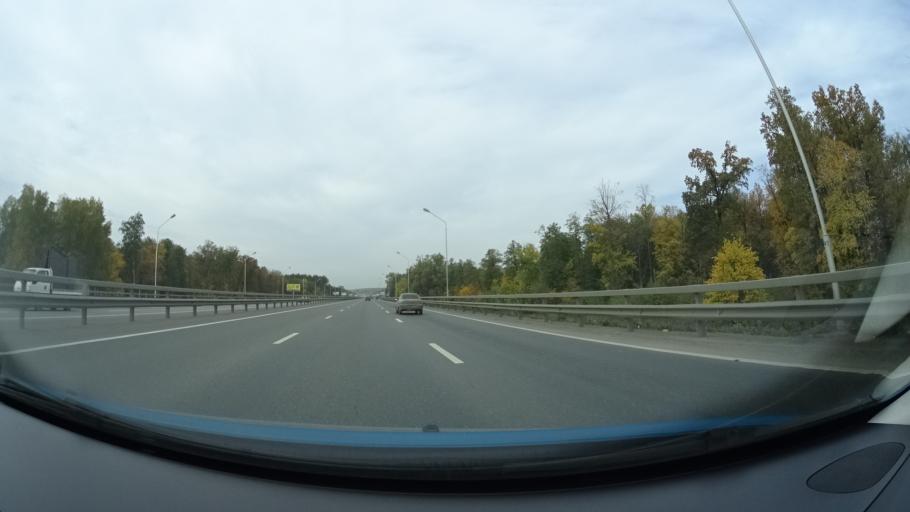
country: RU
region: Bashkortostan
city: Avdon
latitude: 54.6691
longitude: 55.8441
